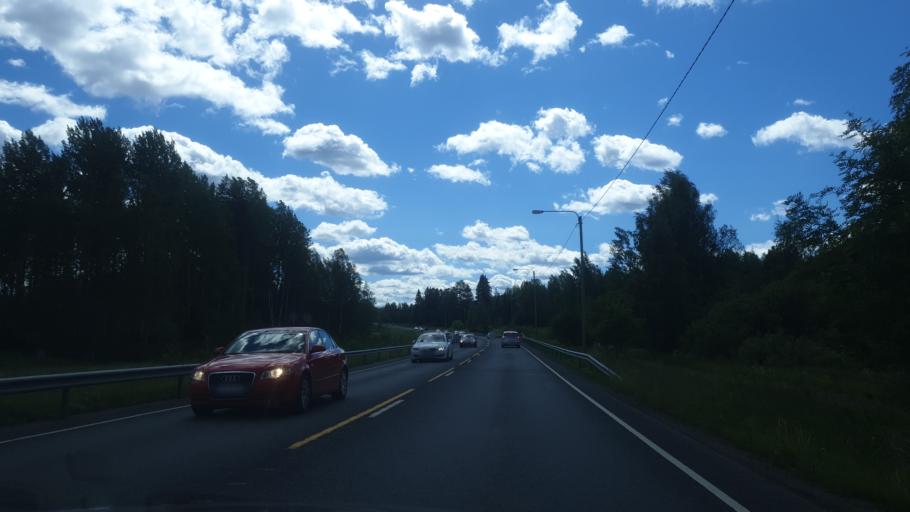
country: FI
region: Northern Savo
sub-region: Varkaus
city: Leppaevirta
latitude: 62.6393
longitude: 27.6097
